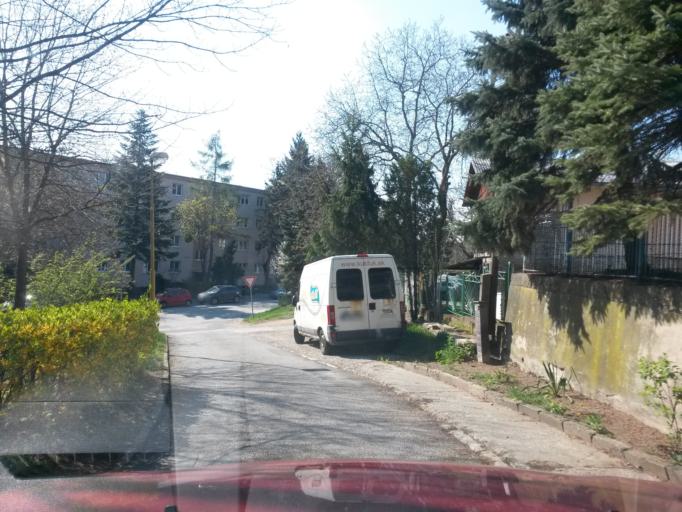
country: SK
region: Kosicky
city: Kosice
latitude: 48.7471
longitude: 21.2416
